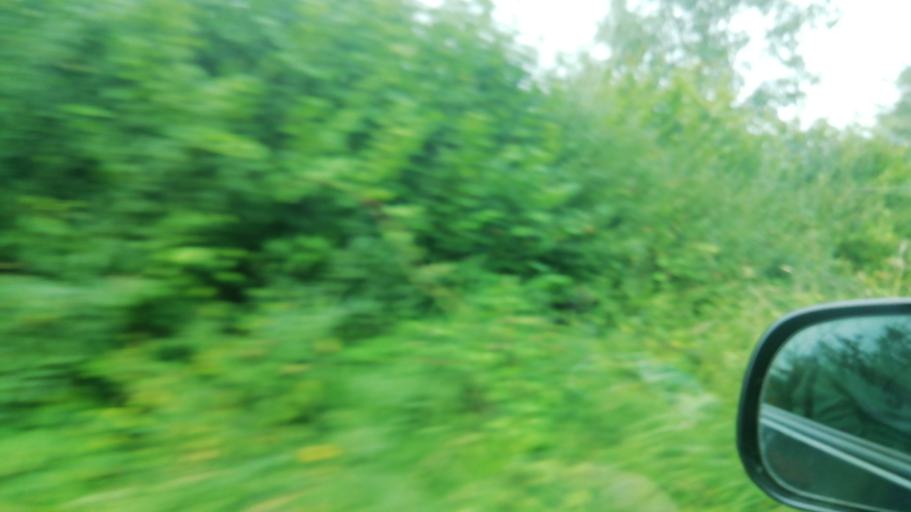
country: IE
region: Munster
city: Fethard
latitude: 52.5843
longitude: -7.5908
